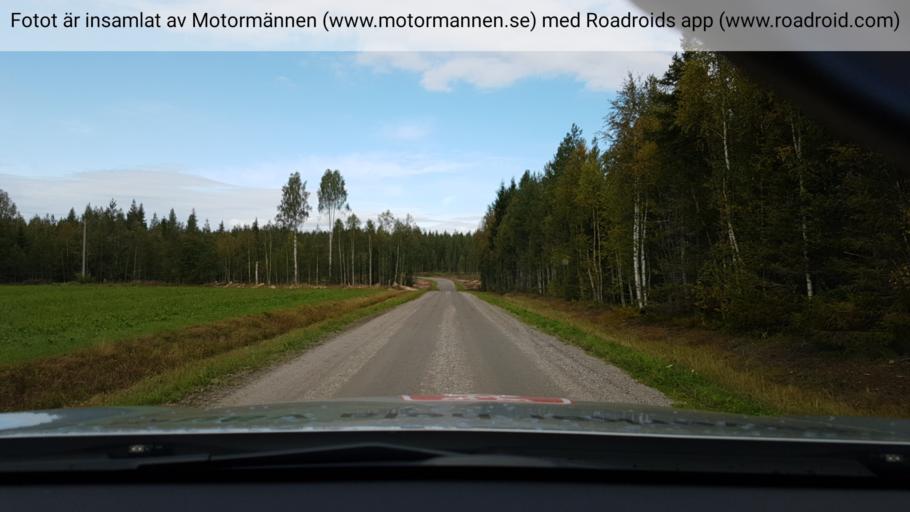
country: SE
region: Vaesterbotten
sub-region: Skelleftea Kommun
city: Backa
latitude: 65.1565
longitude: 21.1581
